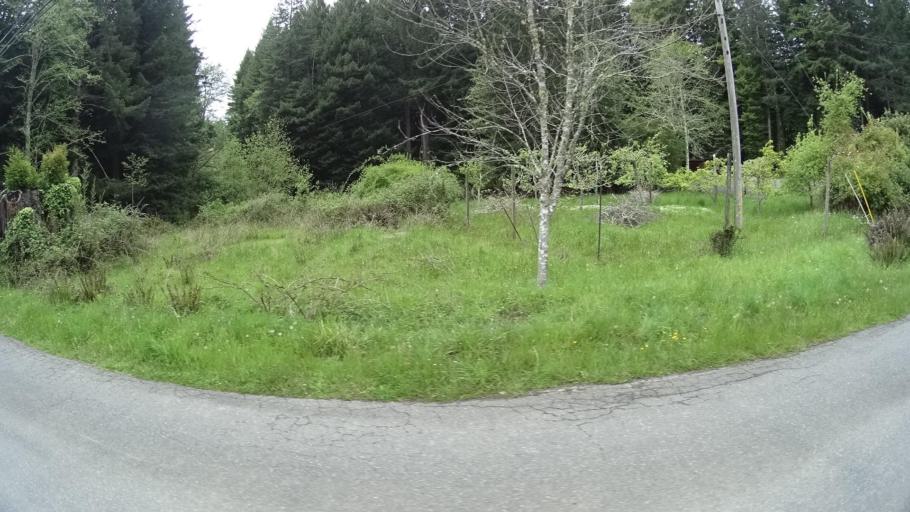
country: US
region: California
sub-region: Humboldt County
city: Bayside
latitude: 40.7985
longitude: -124.0360
